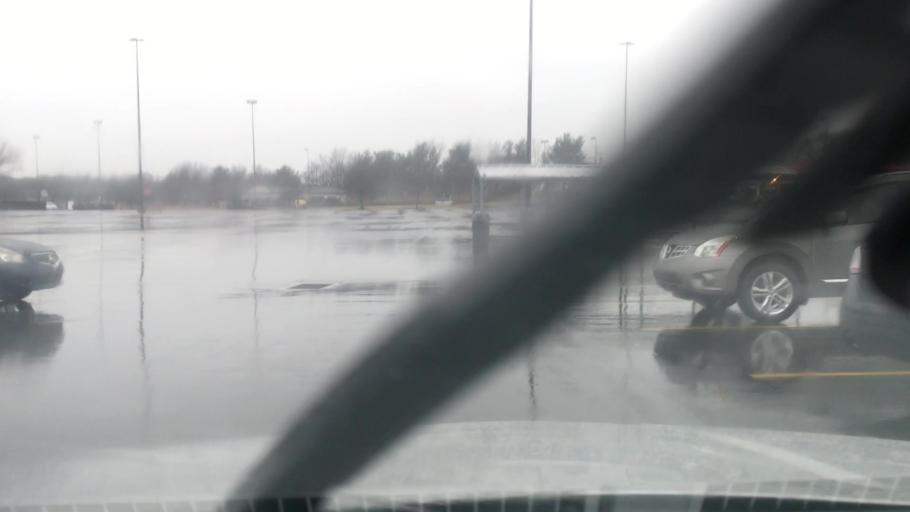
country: US
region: Pennsylvania
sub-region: Bucks County
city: Eddington
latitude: 40.0928
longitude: -74.9596
